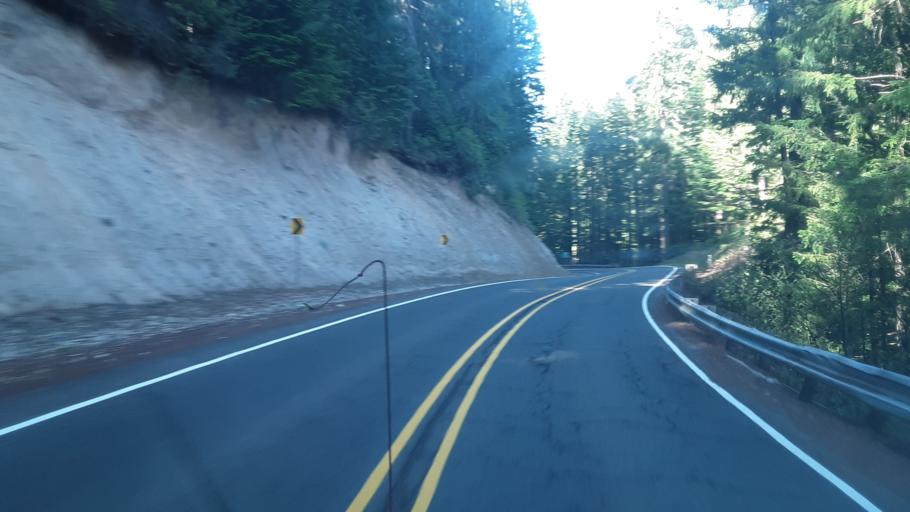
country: US
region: Oregon
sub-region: Jackson County
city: Shady Cove
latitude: 42.9256
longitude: -122.4261
